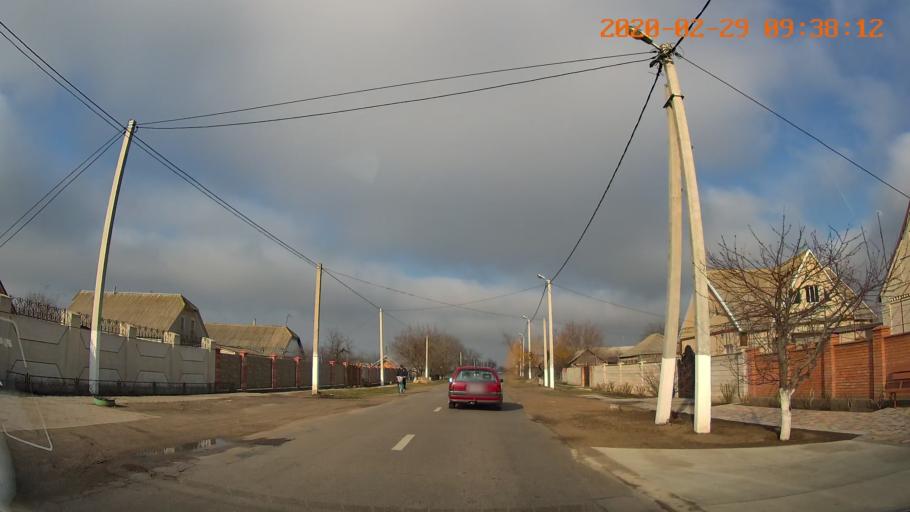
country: MD
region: Telenesti
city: Dnestrovsc
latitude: 46.6299
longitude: 29.8695
